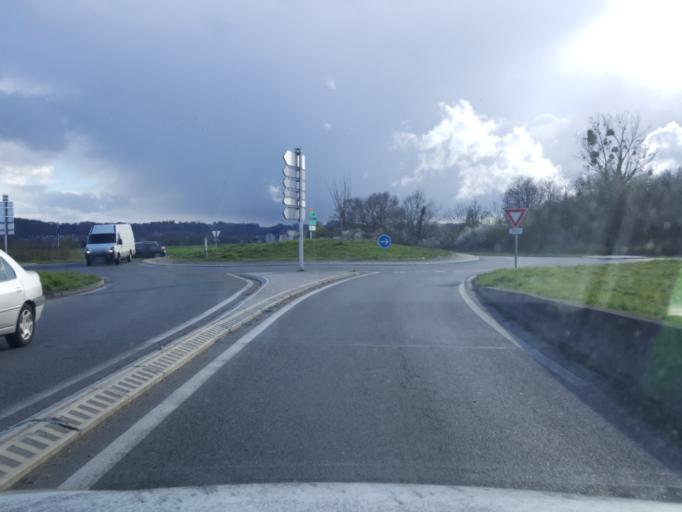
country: FR
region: Picardie
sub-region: Departement de l'Oise
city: Auneuil
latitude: 49.3890
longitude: 2.0095
